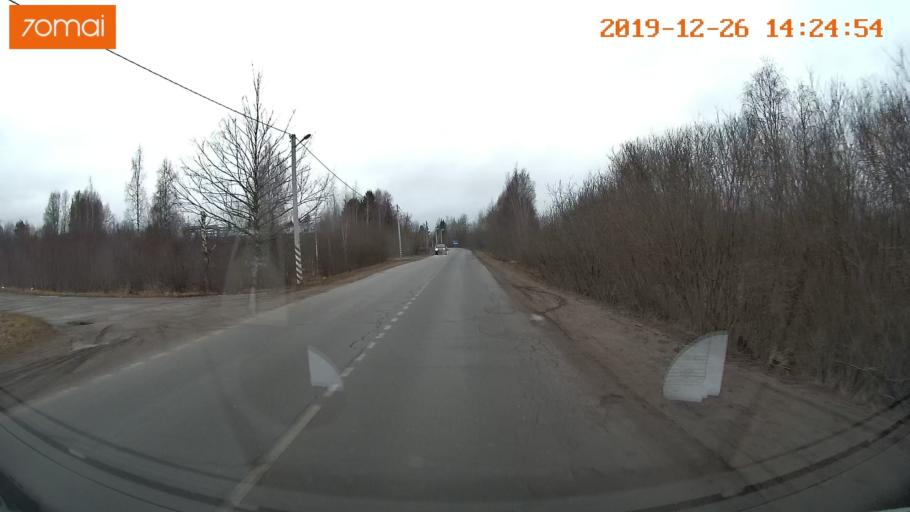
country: RU
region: Jaroslavl
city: Poshekhon'ye
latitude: 58.4969
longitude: 39.1001
